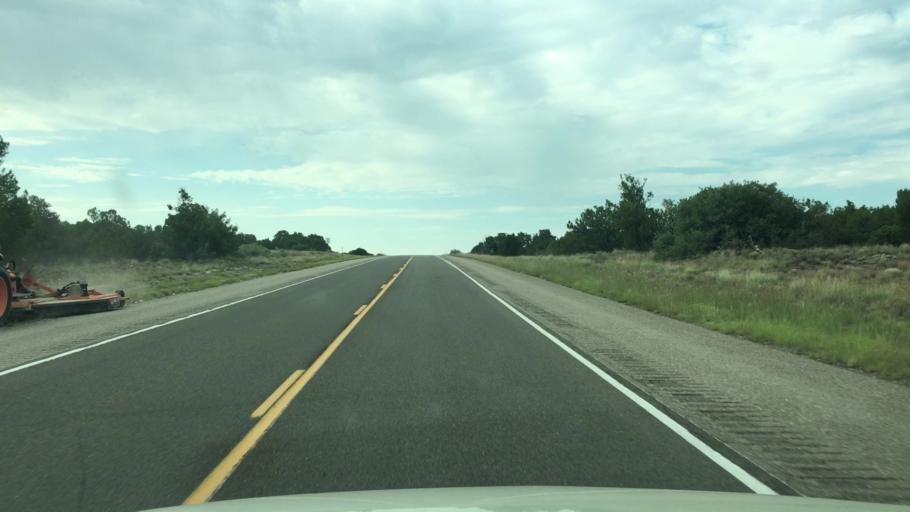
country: US
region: New Mexico
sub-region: Santa Fe County
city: Eldorado at Santa Fe
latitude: 35.2266
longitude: -105.8022
